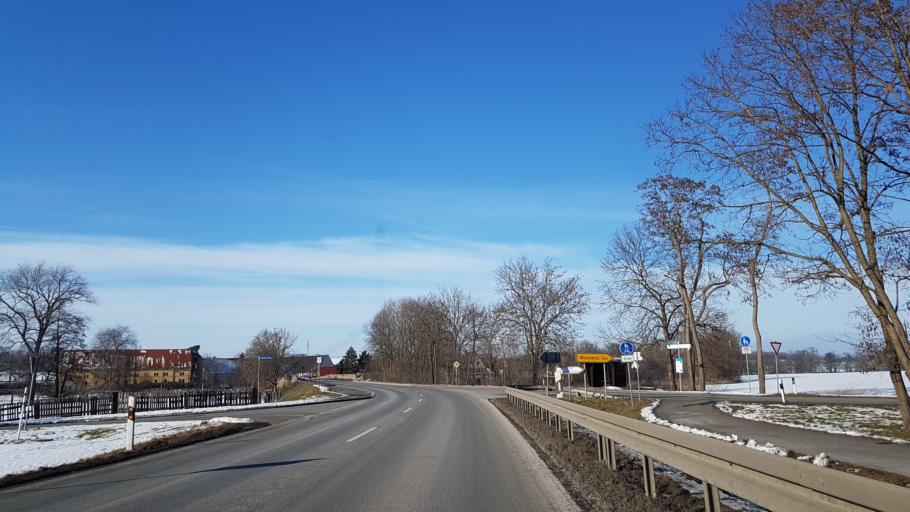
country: DE
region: Thuringia
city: Nobitz
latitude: 50.9821
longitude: 12.4796
